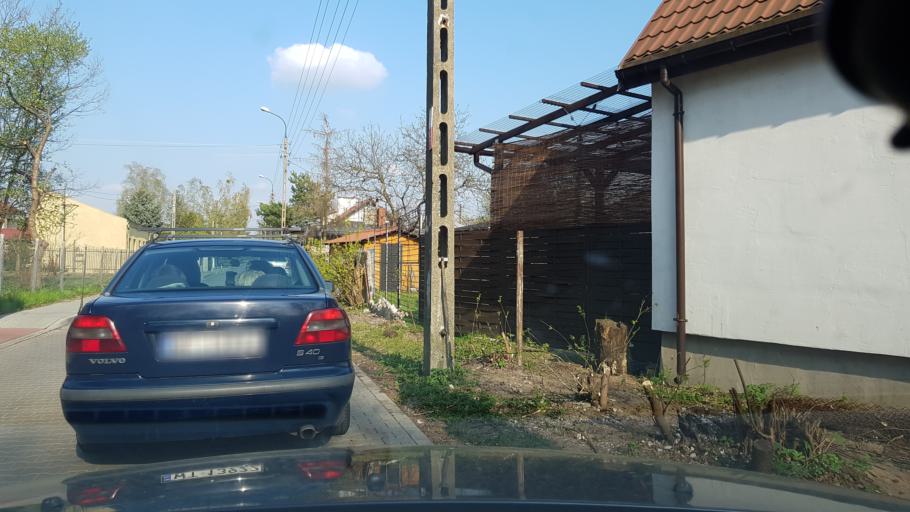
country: PL
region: Masovian Voivodeship
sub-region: Powiat otwocki
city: Jozefow
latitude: 52.1647
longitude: 21.2144
